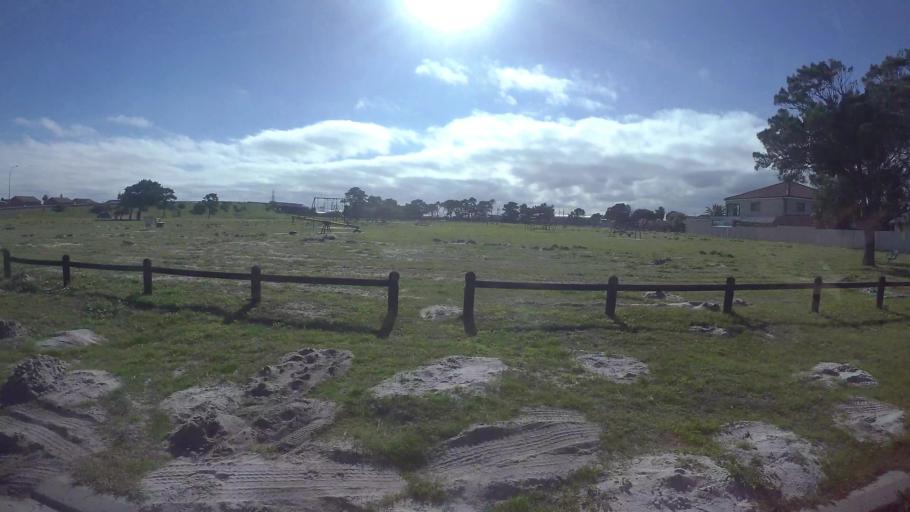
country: ZA
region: Western Cape
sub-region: City of Cape Town
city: Sunset Beach
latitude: -33.8951
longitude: 18.5391
